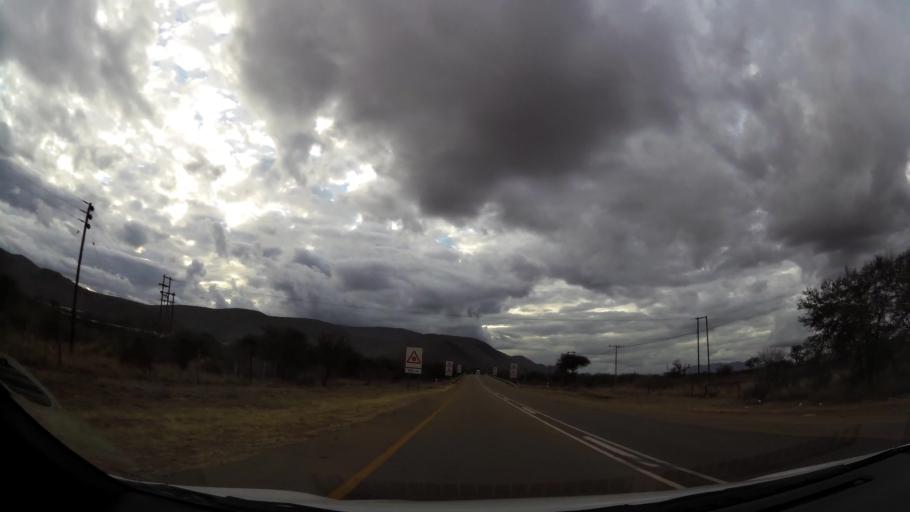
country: ZA
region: Limpopo
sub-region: Waterberg District Municipality
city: Mokopane
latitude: -24.2797
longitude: 28.9790
